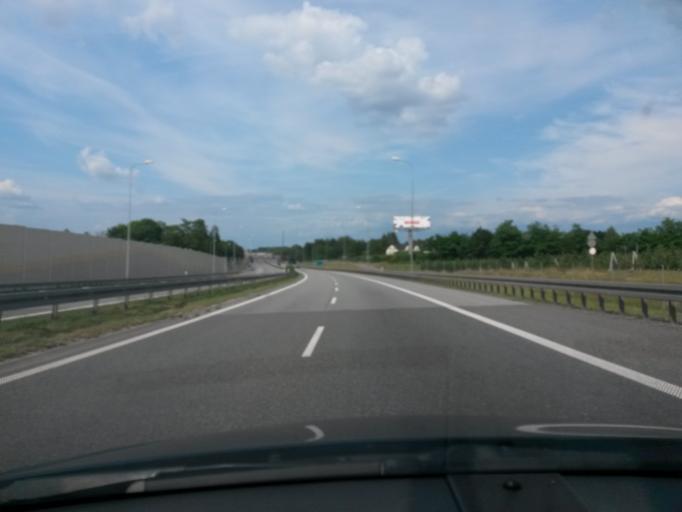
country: PL
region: Lodz Voivodeship
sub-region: Powiat skierniewicki
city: Kowiesy
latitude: 51.8849
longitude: 20.4133
